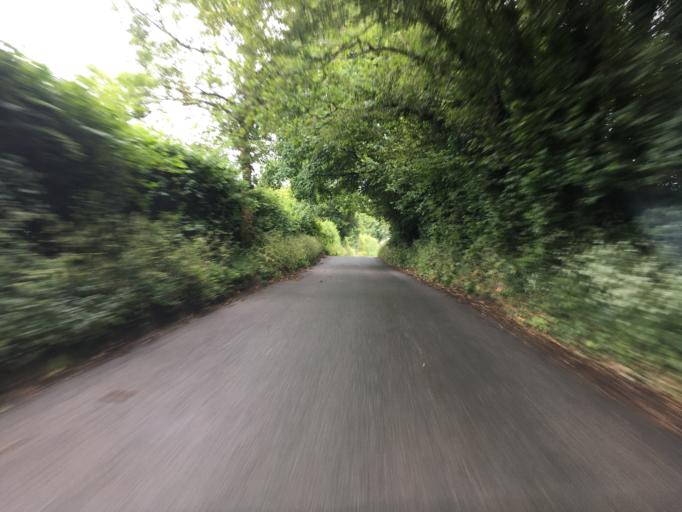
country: GB
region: England
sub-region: Gloucestershire
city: Shurdington
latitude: 51.8192
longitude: -2.1001
